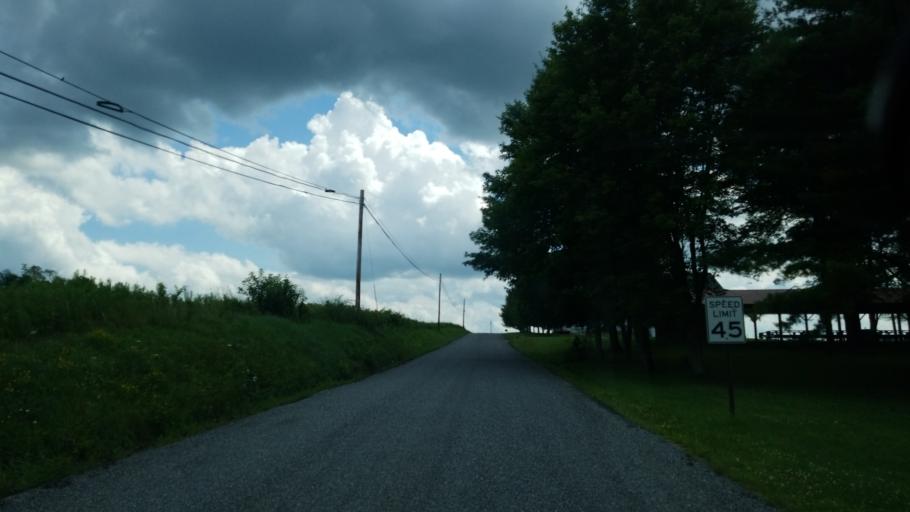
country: US
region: Pennsylvania
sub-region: Jefferson County
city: Brookville
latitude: 41.2373
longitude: -79.0117
